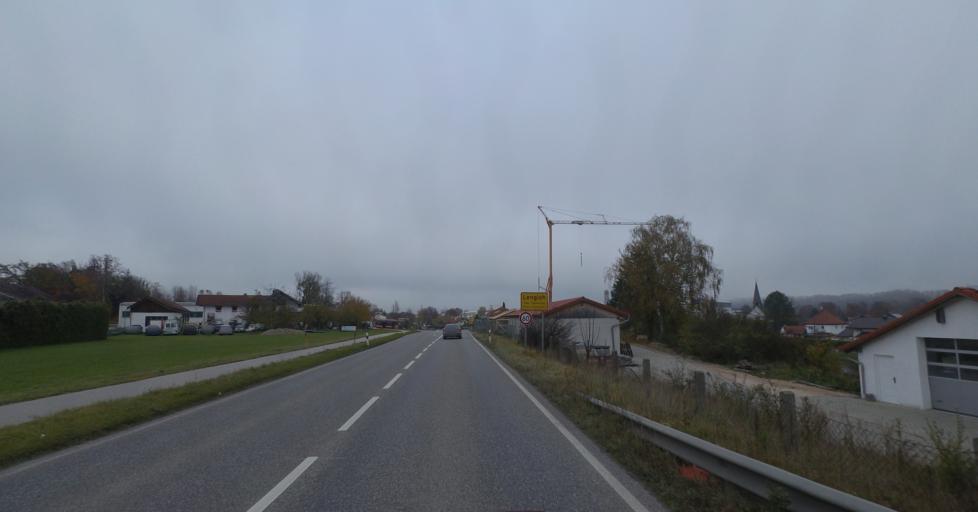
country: DE
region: Bavaria
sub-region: Upper Bavaria
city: Tacherting
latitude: 48.0545
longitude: 12.5691
